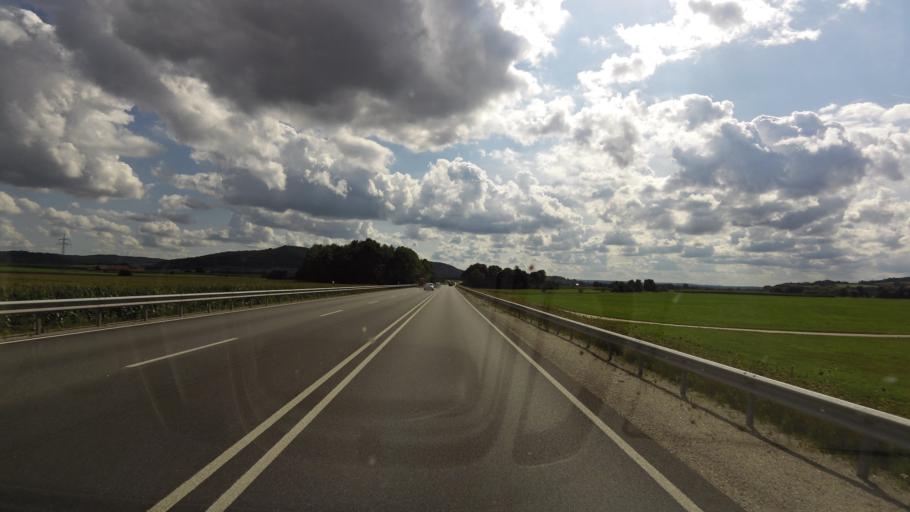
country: DE
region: Bavaria
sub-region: Upper Palatinate
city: Runding
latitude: 49.2310
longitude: 12.7305
